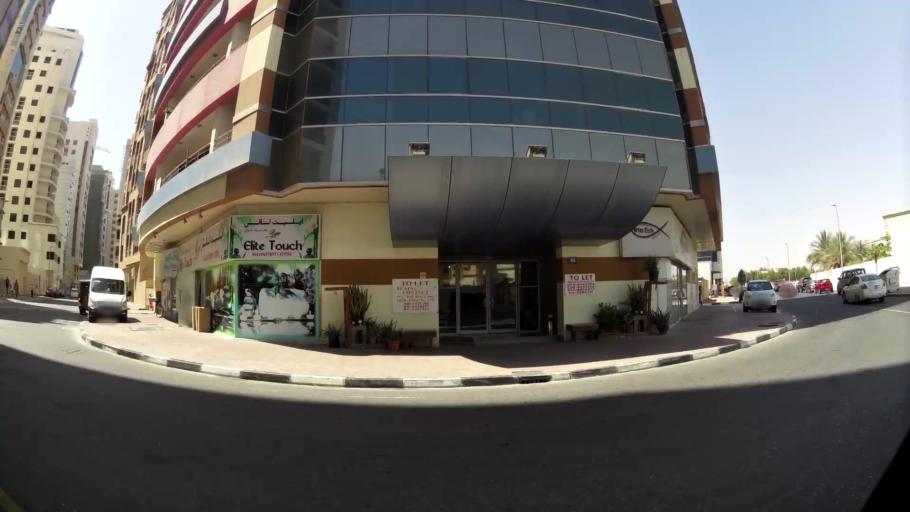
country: AE
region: Dubai
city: Dubai
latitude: 25.1091
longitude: 55.2043
